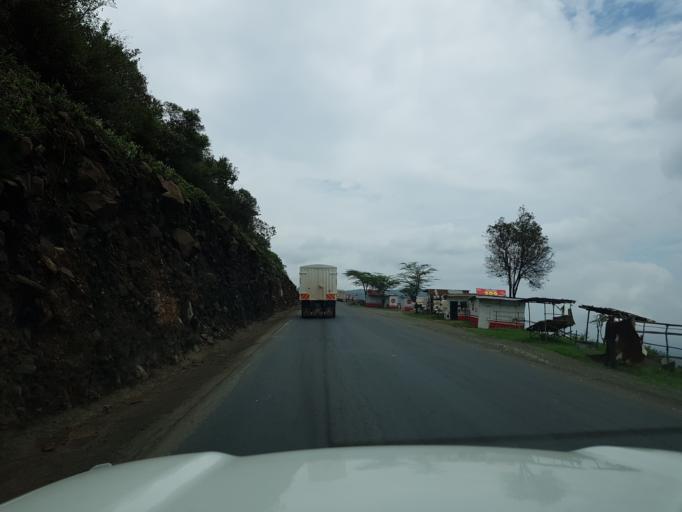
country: KE
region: Kiambu
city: Limuru
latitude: -1.0500
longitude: 36.6021
